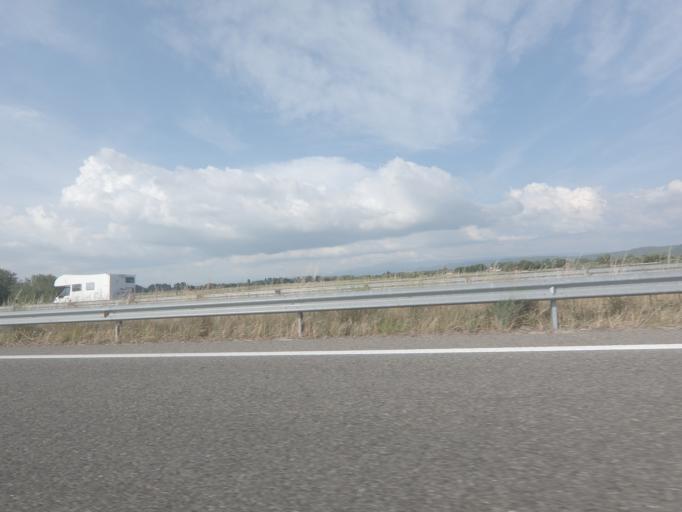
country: ES
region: Galicia
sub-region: Provincia de Ourense
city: Xinzo de Limia
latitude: 42.0885
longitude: -7.7211
